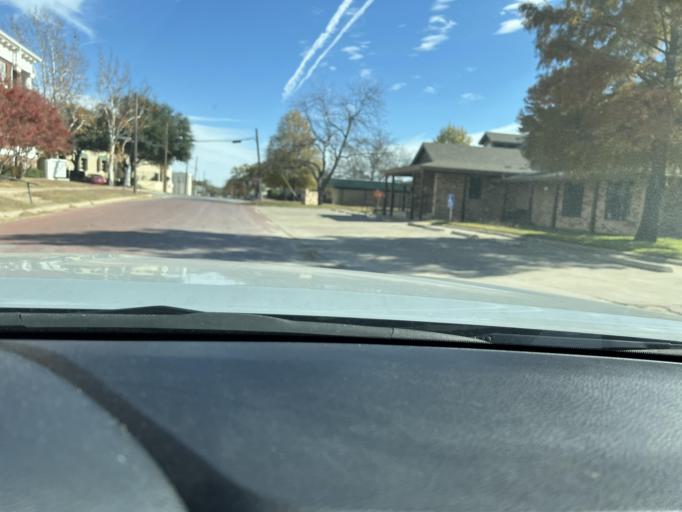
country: US
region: Texas
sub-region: Eastland County
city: Eastland
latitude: 32.3995
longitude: -98.8223
